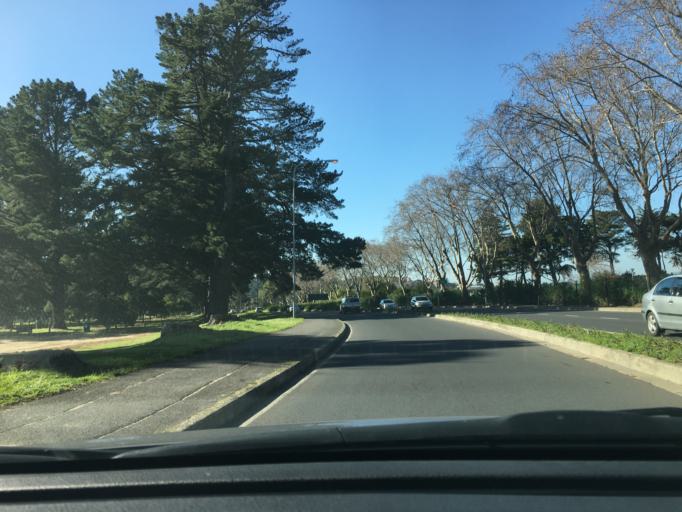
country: ZA
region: Western Cape
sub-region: City of Cape Town
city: Bergvliet
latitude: -34.0192
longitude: 18.4477
